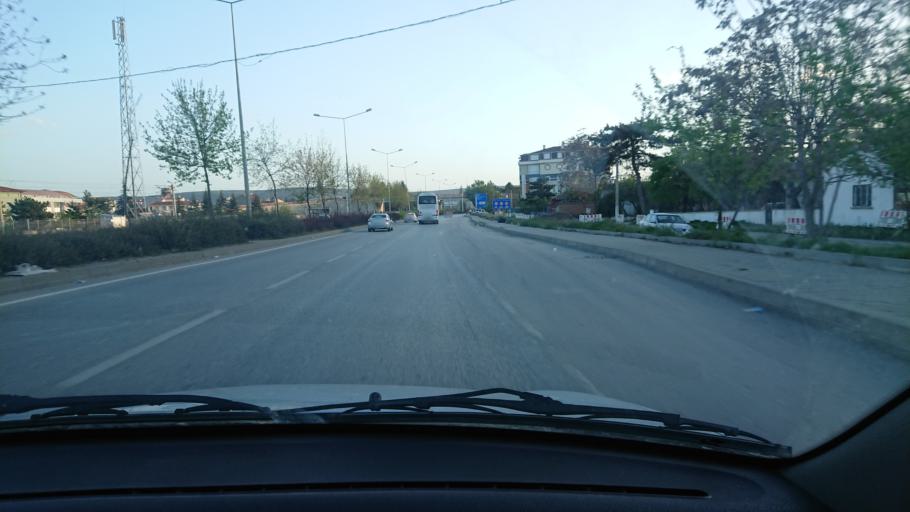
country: TR
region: Eskisehir
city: Eskisehir
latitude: 39.7711
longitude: 30.4827
